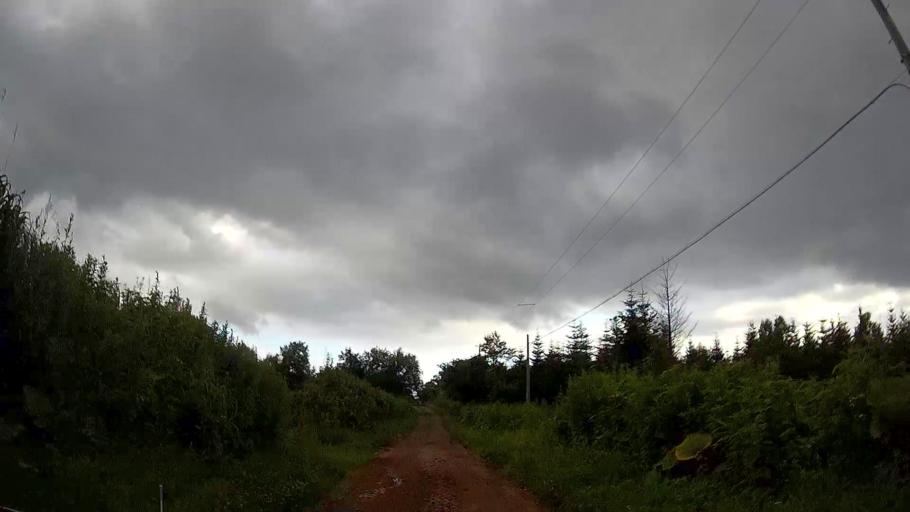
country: JP
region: Hokkaido
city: Nanae
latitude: 42.1261
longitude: 140.4100
